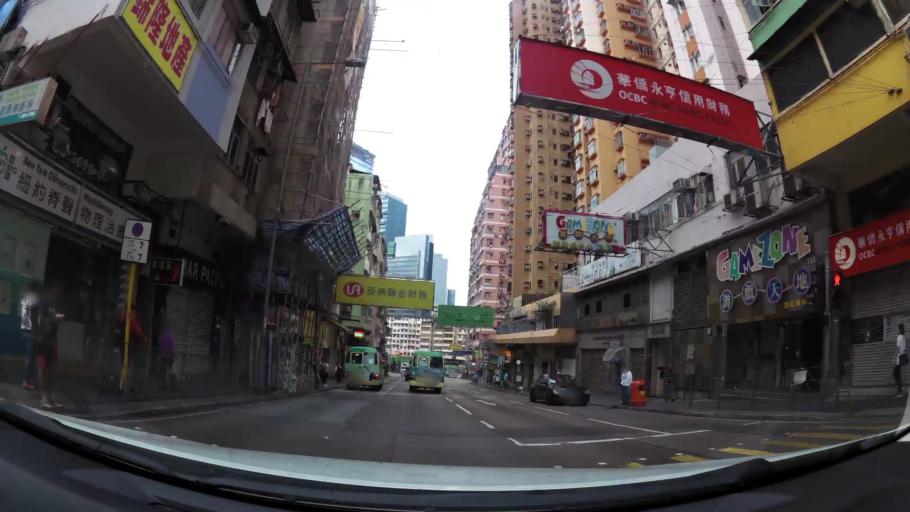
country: HK
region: Kowloon City
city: Kowloon
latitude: 22.3158
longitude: 114.2236
